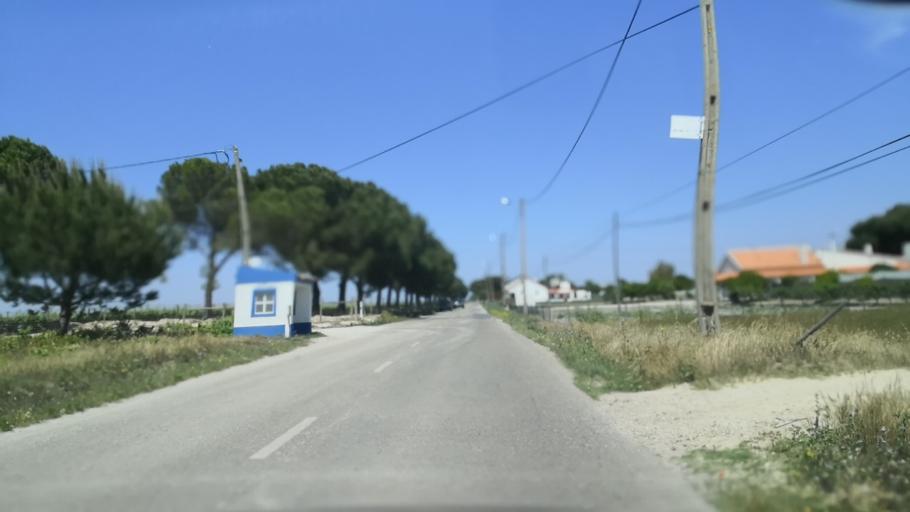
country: PT
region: Santarem
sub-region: Benavente
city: Poceirao
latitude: 38.6755
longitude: -8.7342
